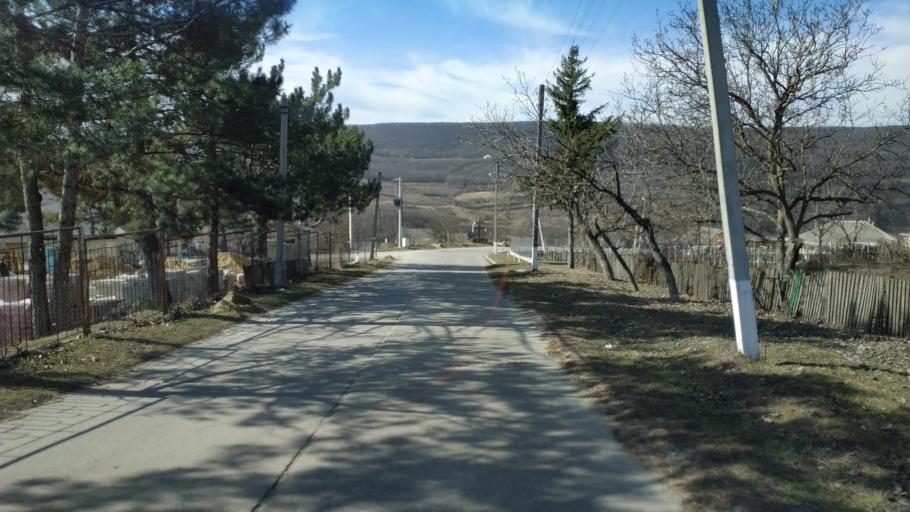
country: MD
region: Nisporeni
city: Nisporeni
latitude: 47.0726
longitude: 28.2629
